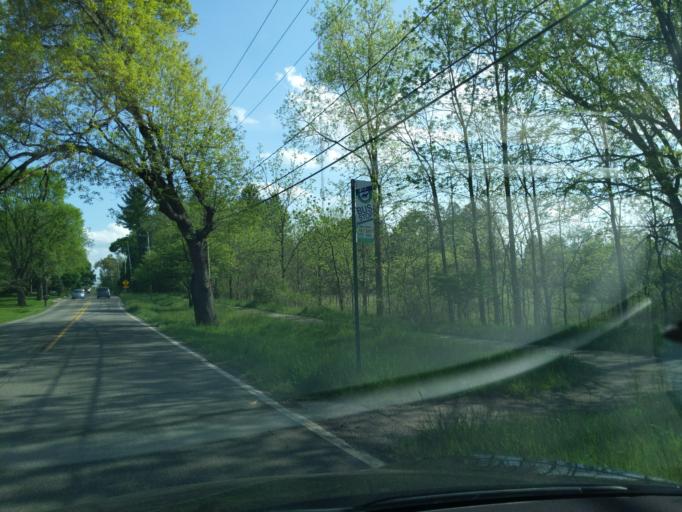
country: US
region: Michigan
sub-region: Ingham County
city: Okemos
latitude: 42.7073
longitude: -84.4104
